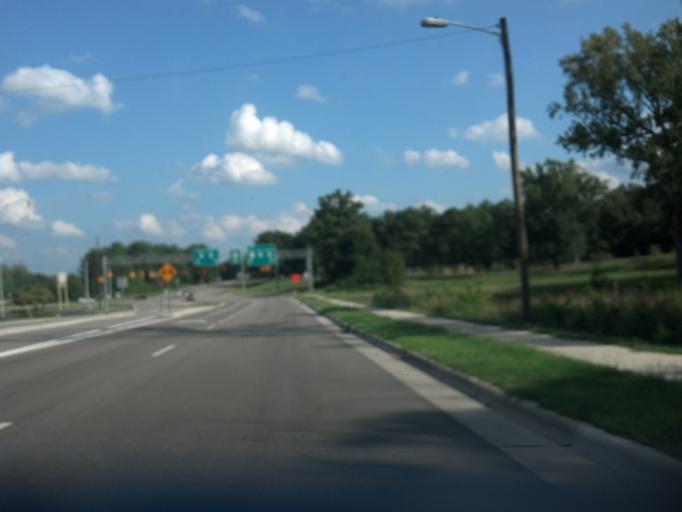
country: US
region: North Carolina
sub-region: Nash County
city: Rocky Mount
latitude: 35.9668
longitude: -77.8068
